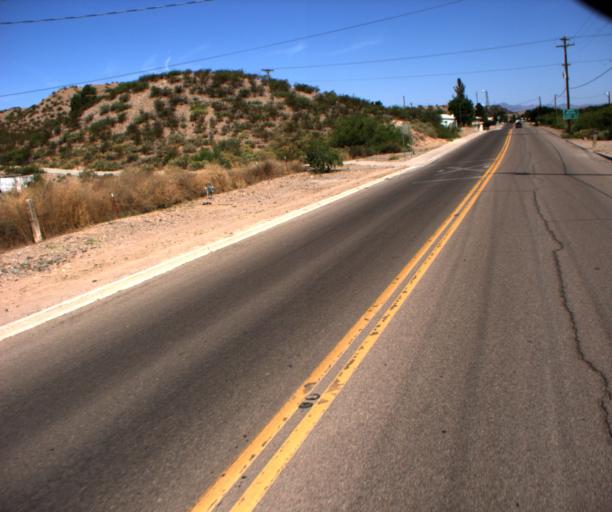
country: US
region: Arizona
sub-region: Greenlee County
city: Clifton
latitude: 32.7100
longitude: -109.0949
